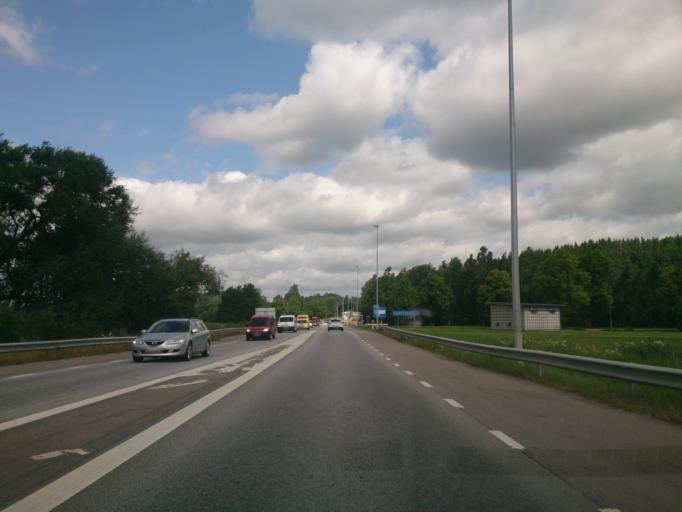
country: SE
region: OEstergoetland
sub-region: Soderkopings Kommun
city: Soederkoeping
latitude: 58.4852
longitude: 16.3113
